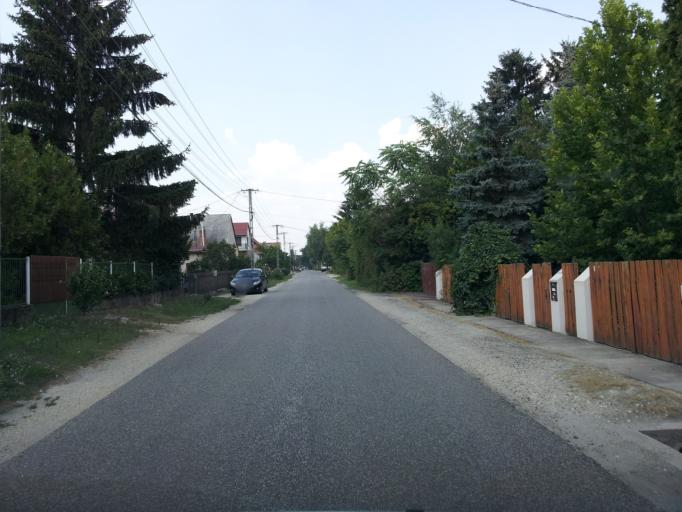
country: HU
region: Pest
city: Szigethalom
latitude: 47.3194
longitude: 19.0156
